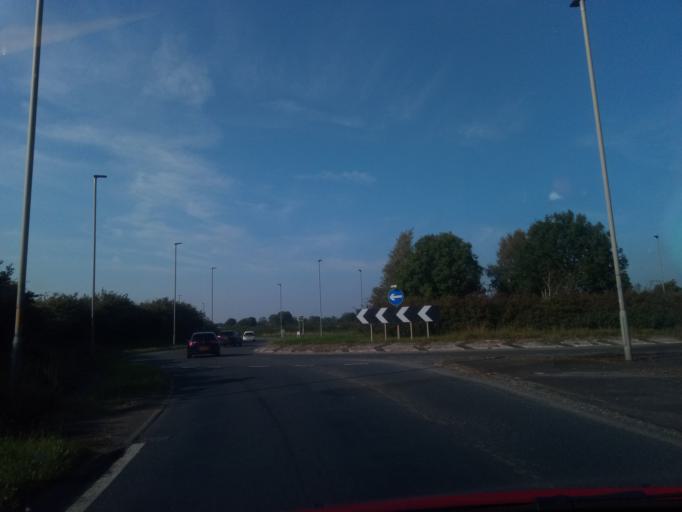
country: GB
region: England
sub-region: North Yorkshire
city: Easingwold
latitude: 54.1039
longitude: -1.1973
